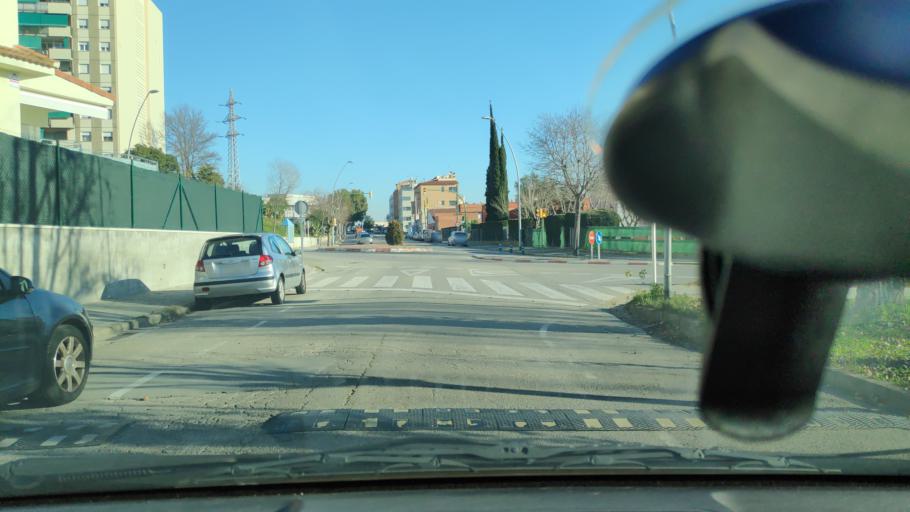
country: ES
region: Catalonia
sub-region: Provincia de Barcelona
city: Sant Quirze del Valles
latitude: 41.5355
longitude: 2.0744
